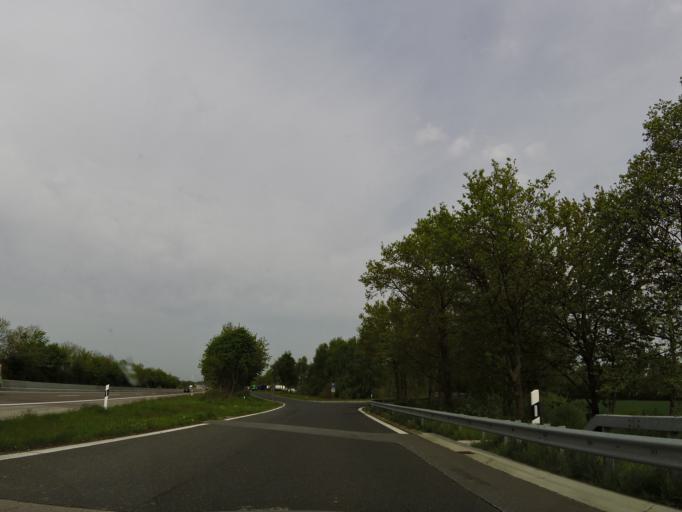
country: DE
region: Schleswig-Holstein
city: Horst
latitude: 53.8277
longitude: 9.6355
